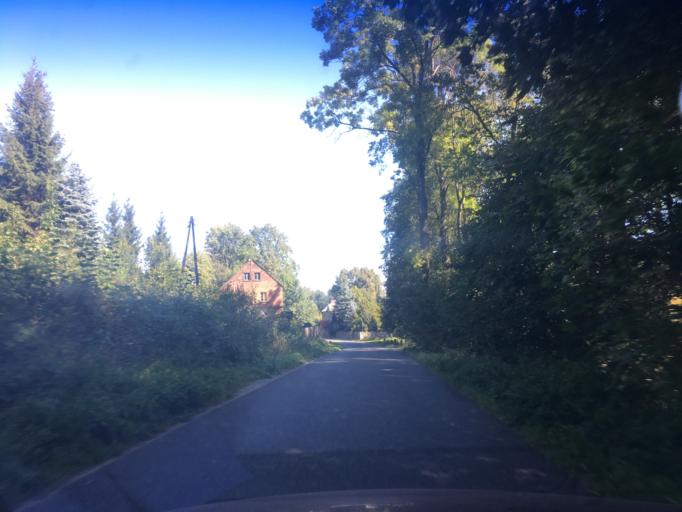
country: PL
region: Lower Silesian Voivodeship
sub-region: Powiat lubanski
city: Lesna
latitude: 51.0114
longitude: 15.1982
